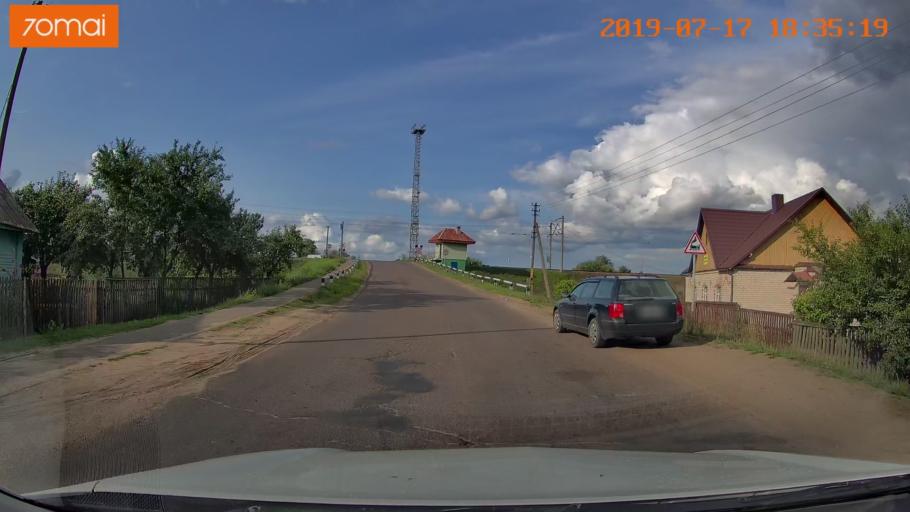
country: BY
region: Mogilev
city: Asipovichy
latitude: 53.2918
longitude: 28.6574
